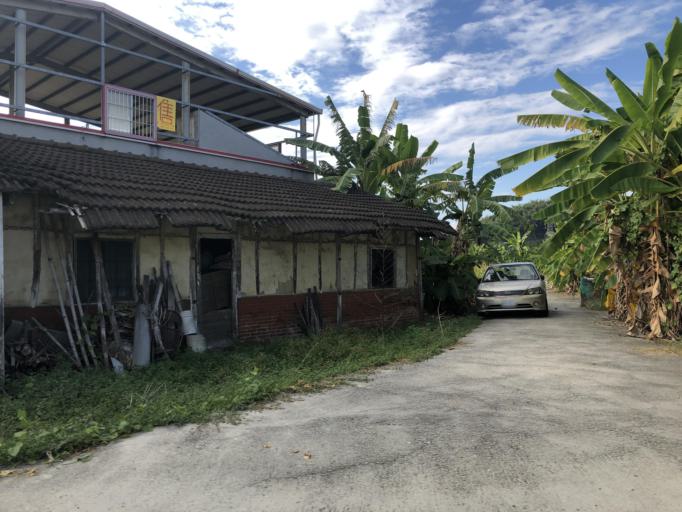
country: TW
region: Taiwan
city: Yujing
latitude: 23.0399
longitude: 120.4221
